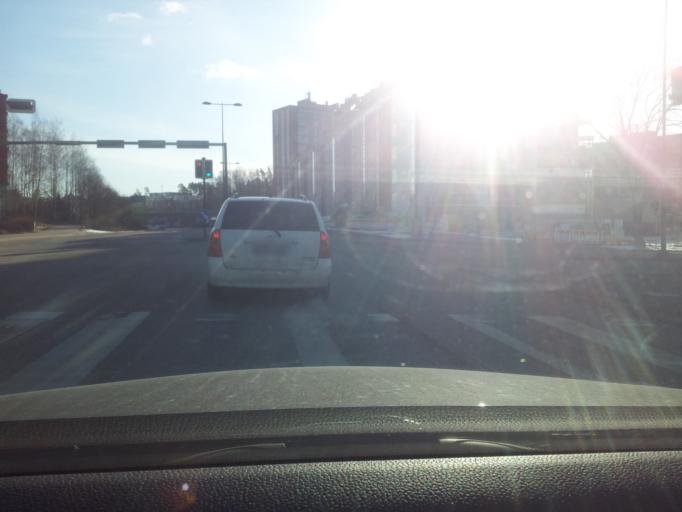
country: FI
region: Uusimaa
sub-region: Helsinki
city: Koukkuniemi
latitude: 60.1658
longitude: 24.7319
